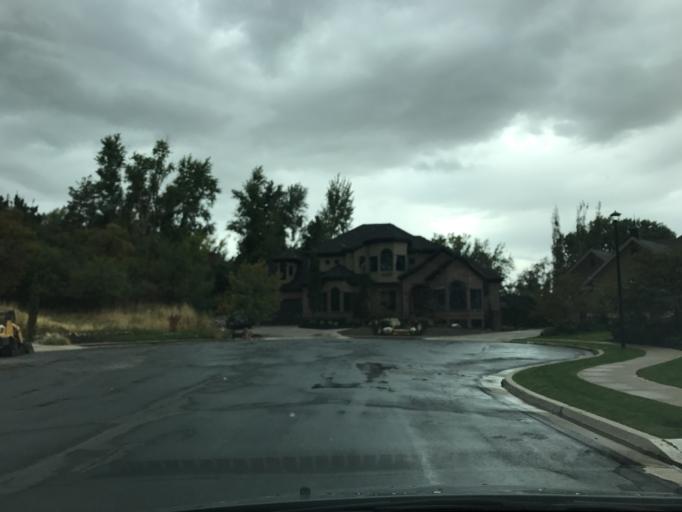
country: US
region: Utah
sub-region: Davis County
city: Fruit Heights
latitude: 41.0136
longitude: -111.9010
